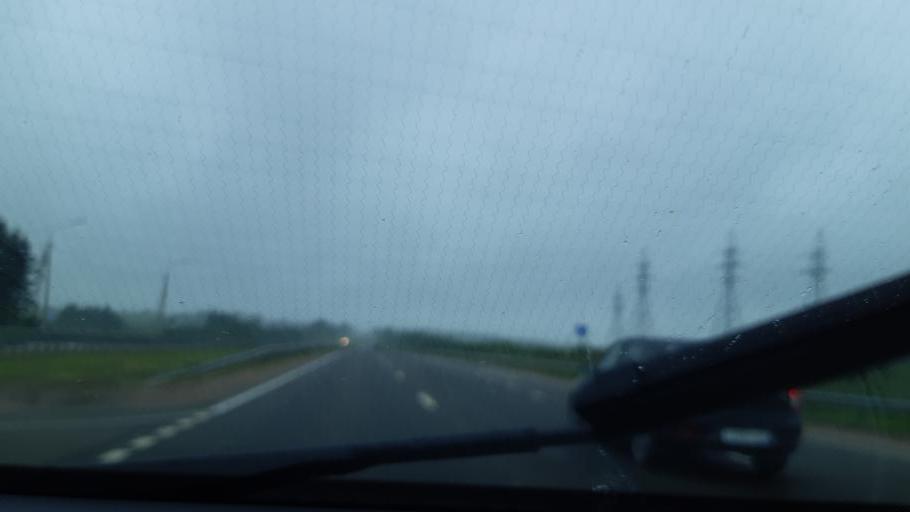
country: RU
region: Smolensk
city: Talashkino
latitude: 54.6602
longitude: 32.1594
